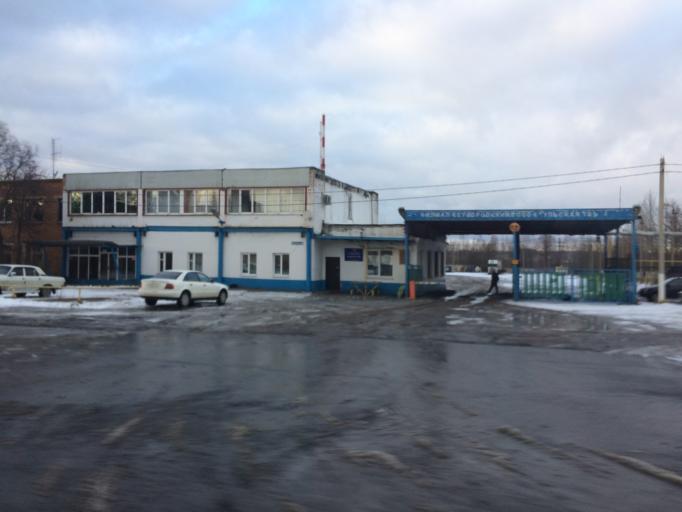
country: RU
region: Tula
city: Ageyevo
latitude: 54.1301
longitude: 36.4658
